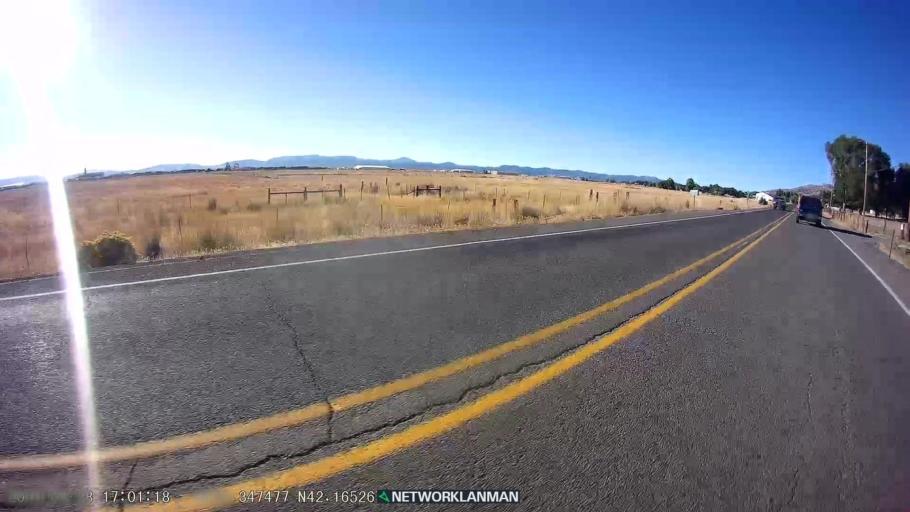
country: US
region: Oregon
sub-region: Lake County
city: Lakeview
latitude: 42.1655
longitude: -120.3474
